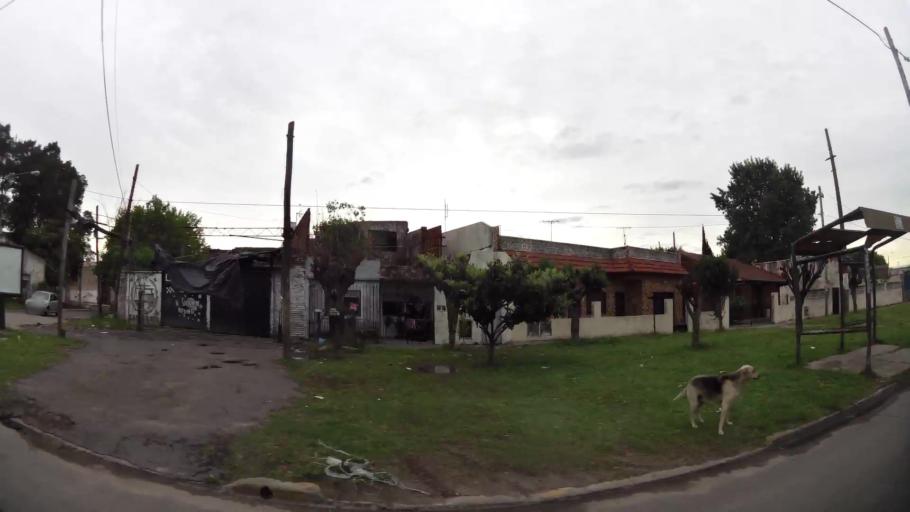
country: AR
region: Buenos Aires
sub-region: Partido de Lanus
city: Lanus
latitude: -34.7187
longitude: -58.3502
